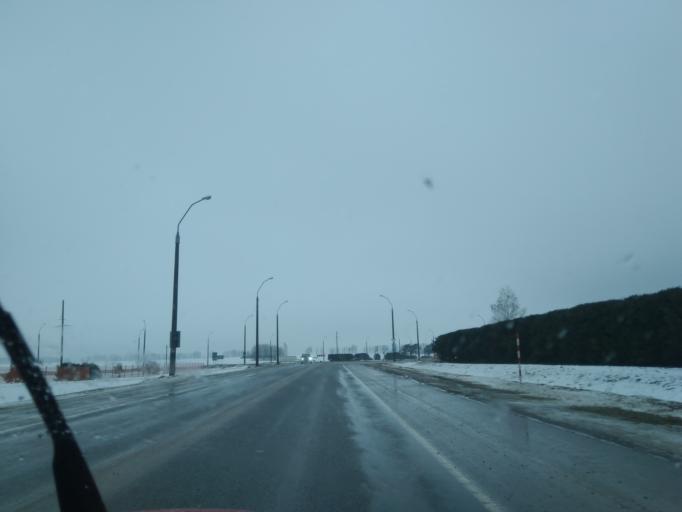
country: BY
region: Minsk
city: Nyasvizh
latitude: 53.2378
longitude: 26.6365
